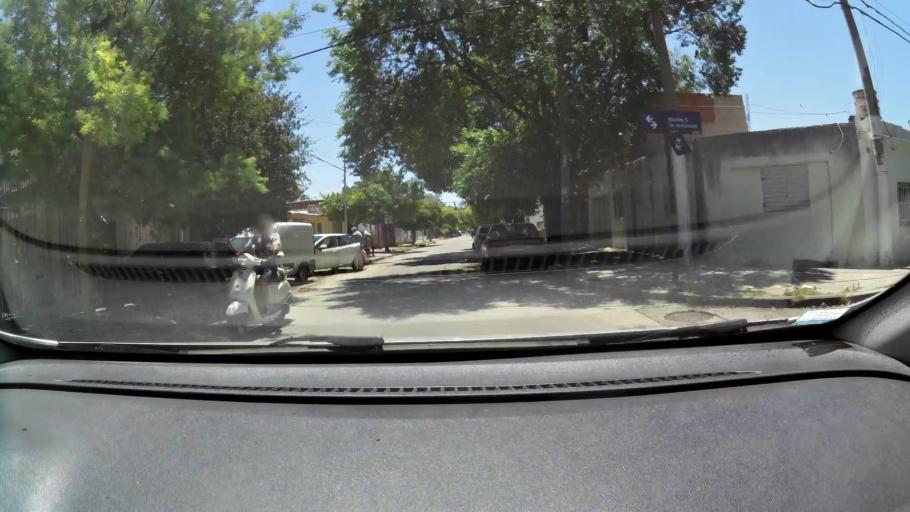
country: AR
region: Cordoba
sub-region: Departamento de Capital
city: Cordoba
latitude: -31.3851
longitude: -64.1304
